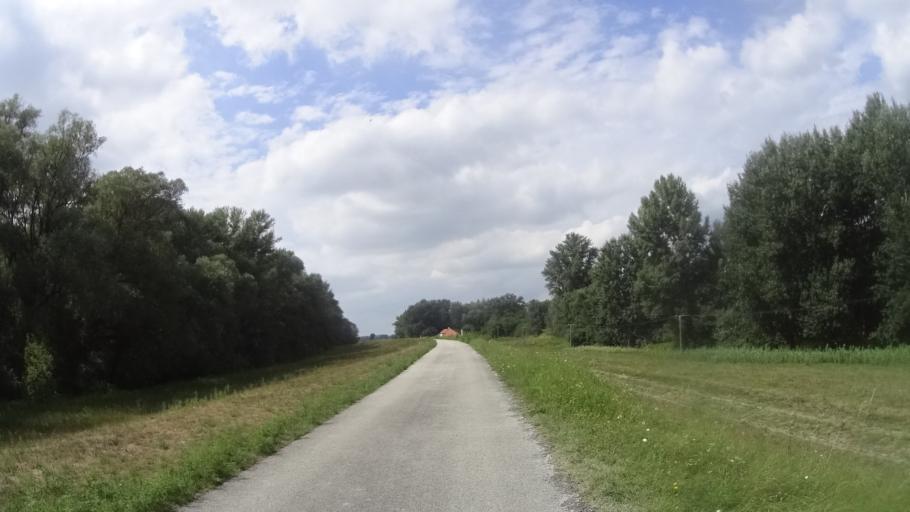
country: SK
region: Trnavsky
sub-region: Okres Dunajska Streda
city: Velky Meder
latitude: 47.7902
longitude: 17.6912
